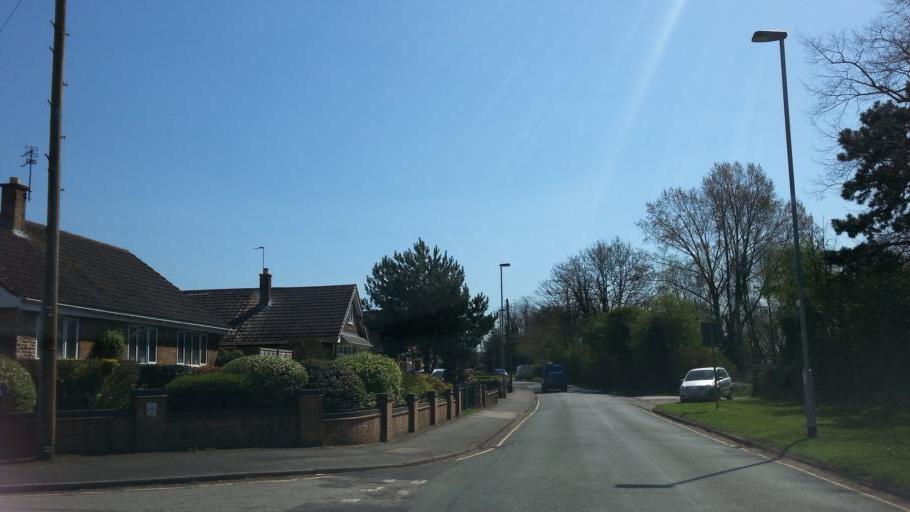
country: GB
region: England
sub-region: Staffordshire
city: Cannock
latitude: 52.6819
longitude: -2.0484
